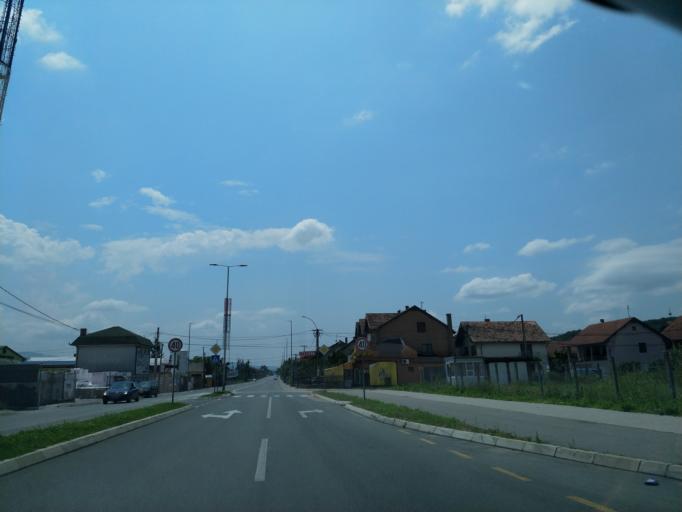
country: RS
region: Central Serbia
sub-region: Rasinski Okrug
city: Krusevac
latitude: 43.5559
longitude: 21.3317
